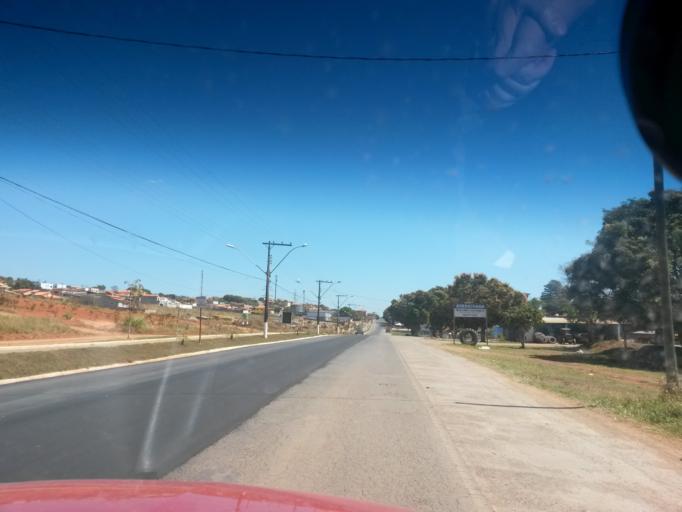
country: BR
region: Minas Gerais
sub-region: Bambui
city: Bambui
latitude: -20.0154
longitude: -45.9609
